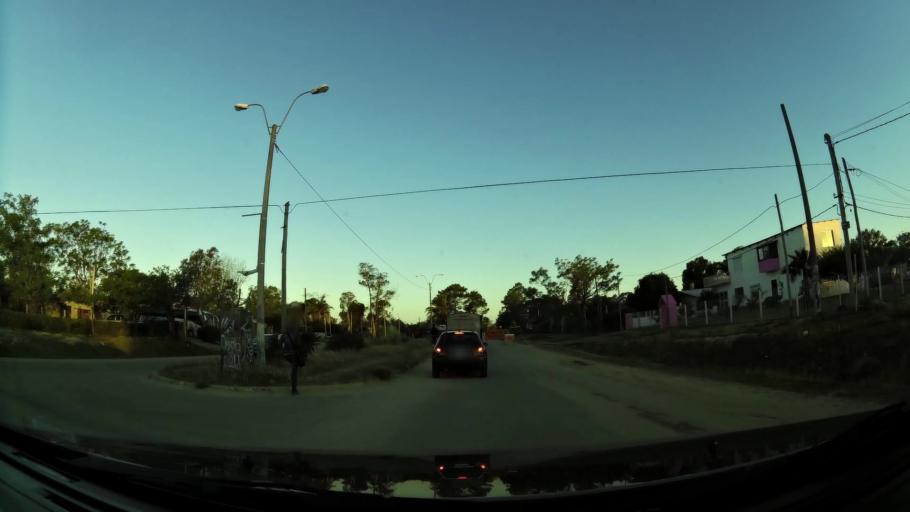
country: UY
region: Canelones
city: Barra de Carrasco
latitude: -34.8459
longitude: -55.9880
